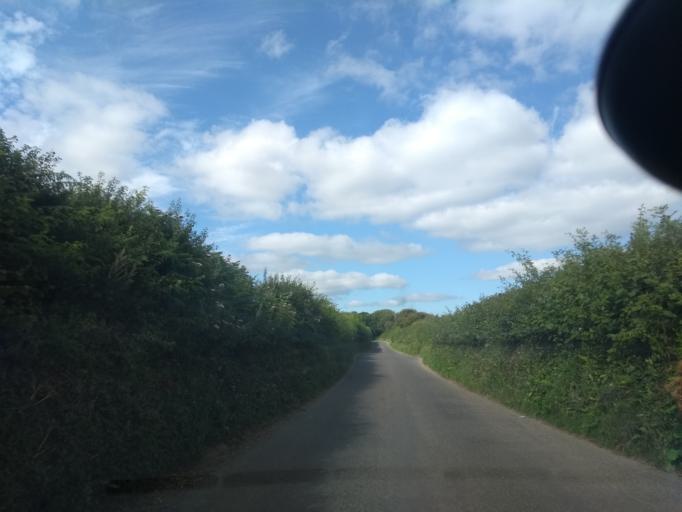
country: GB
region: England
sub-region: Devon
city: Modbury
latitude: 50.3027
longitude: -3.8873
